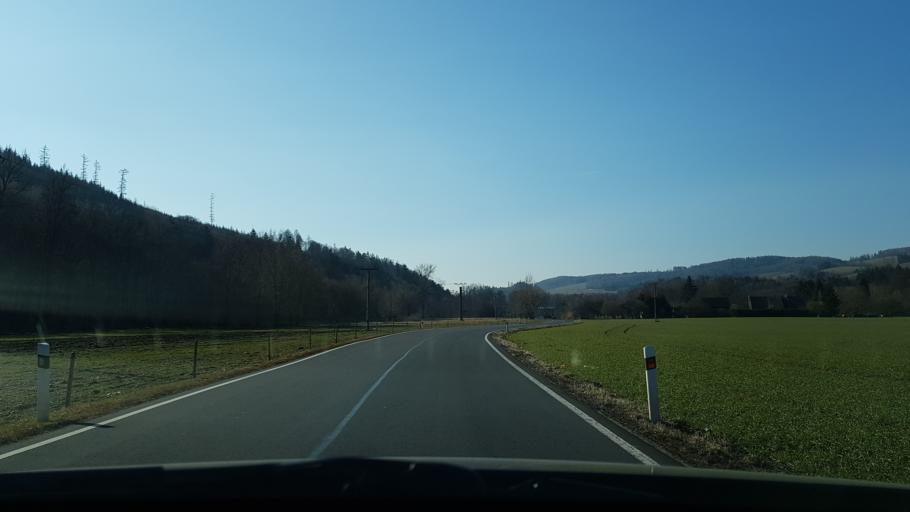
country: CZ
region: Olomoucky
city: Dolni Bohdikov
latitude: 50.0349
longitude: 16.9065
